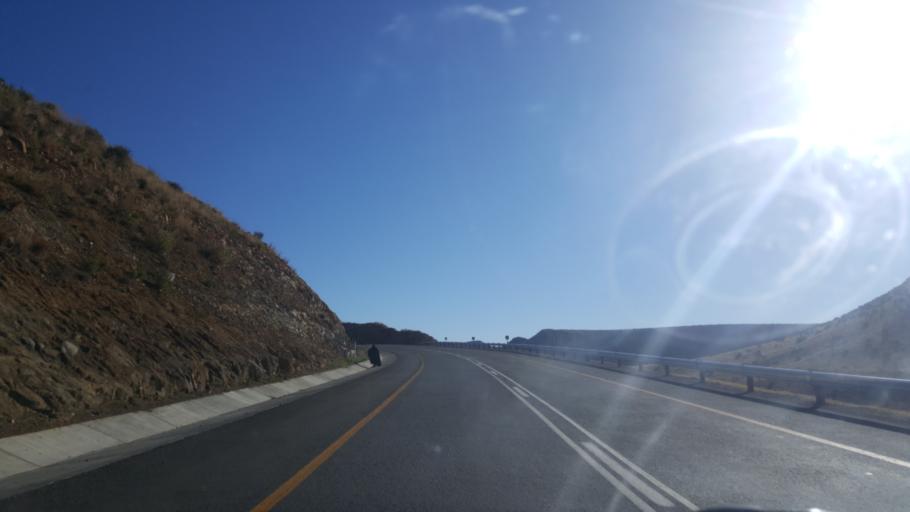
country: ZA
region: Eastern Cape
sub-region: Chris Hani District Municipality
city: Middelburg
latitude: -31.3814
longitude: 25.0334
